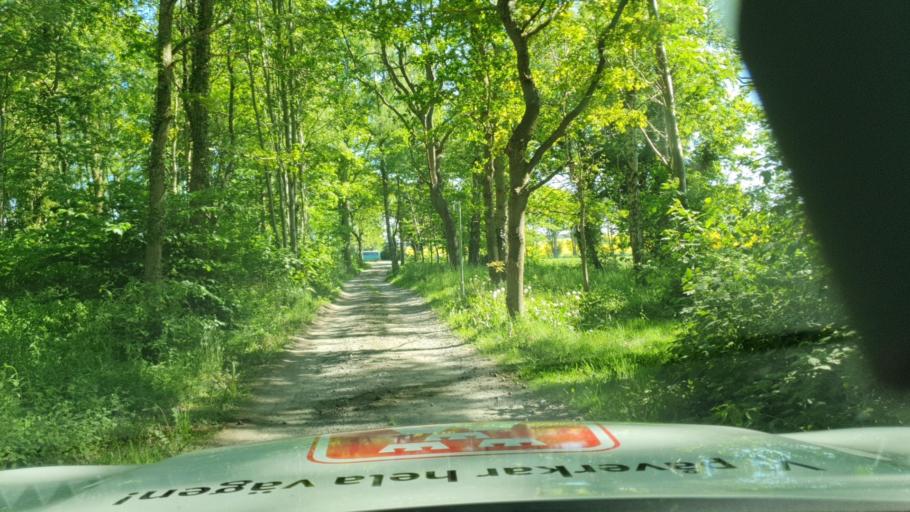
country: SE
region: Skane
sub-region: Simrishamns Kommun
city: Simrishamn
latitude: 55.4938
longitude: 14.2742
